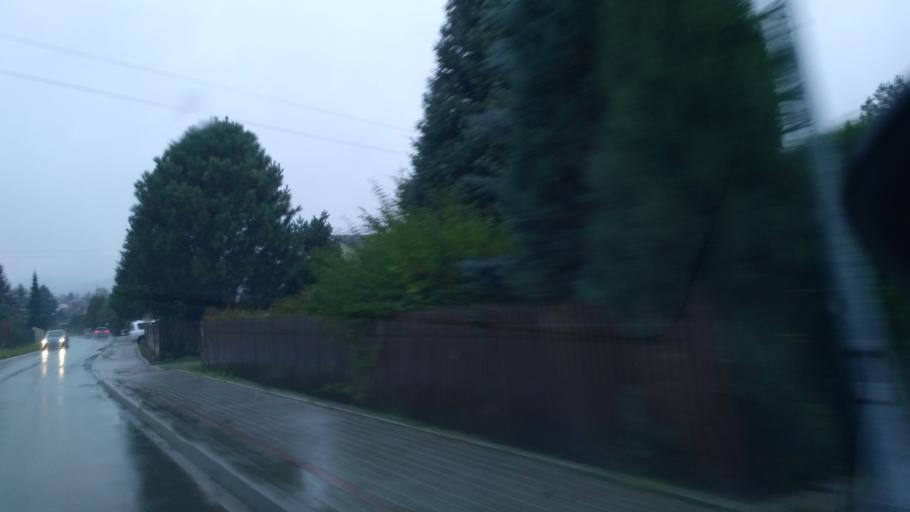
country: PL
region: Subcarpathian Voivodeship
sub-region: Powiat krosnienski
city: Korczyna
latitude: 49.7050
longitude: 21.8119
